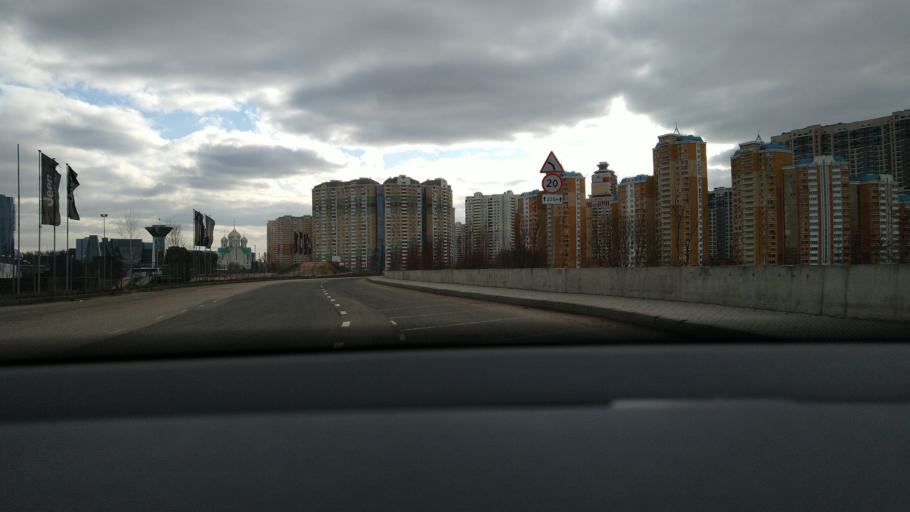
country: RU
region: Moskovskaya
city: Pavshino
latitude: 55.8283
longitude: 37.3808
